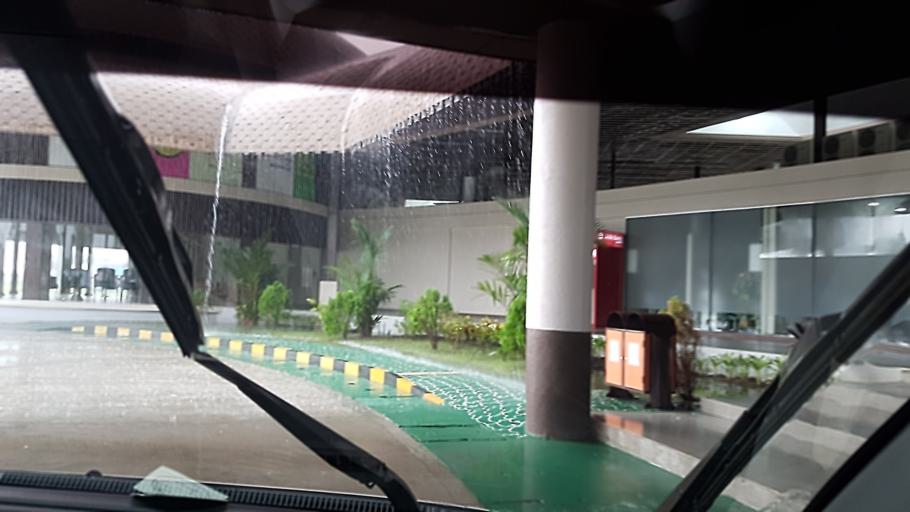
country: MM
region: Yangon
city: Syriam
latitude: 16.7732
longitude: 96.2002
